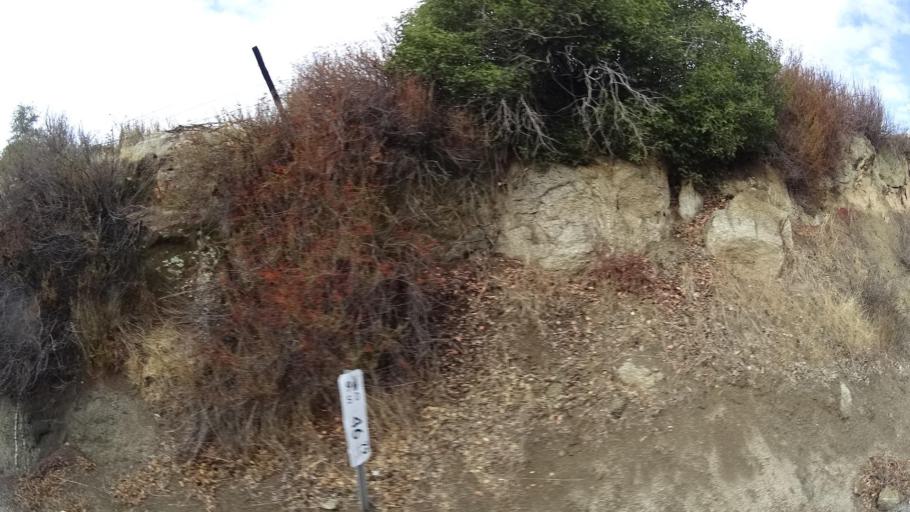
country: MX
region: Baja California
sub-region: Tecate
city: Hacienda Tecate
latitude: 32.5926
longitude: -116.5275
